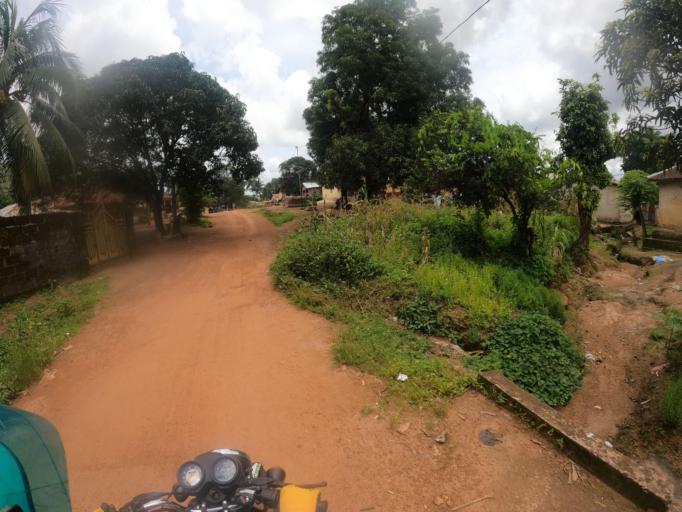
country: SL
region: Northern Province
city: Makeni
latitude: 8.8935
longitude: -12.0518
